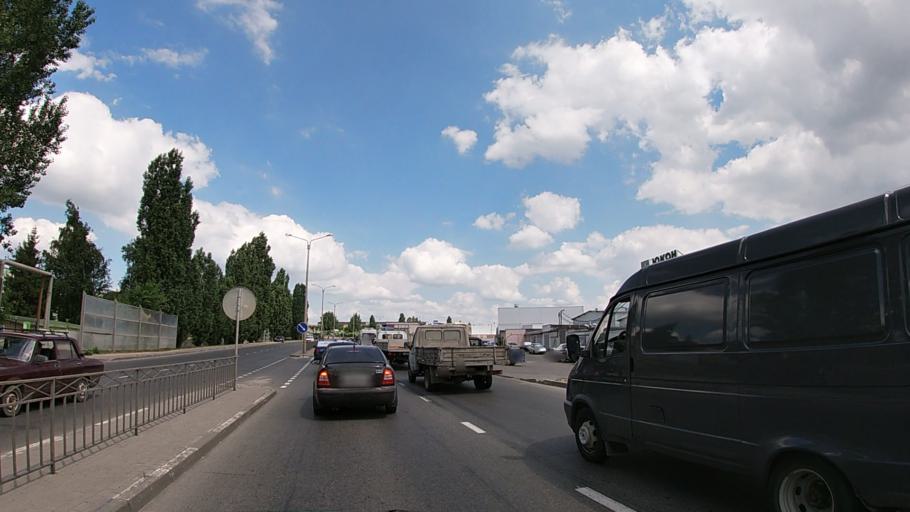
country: RU
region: Belgorod
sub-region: Belgorodskiy Rayon
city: Belgorod
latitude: 50.6101
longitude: 36.5339
